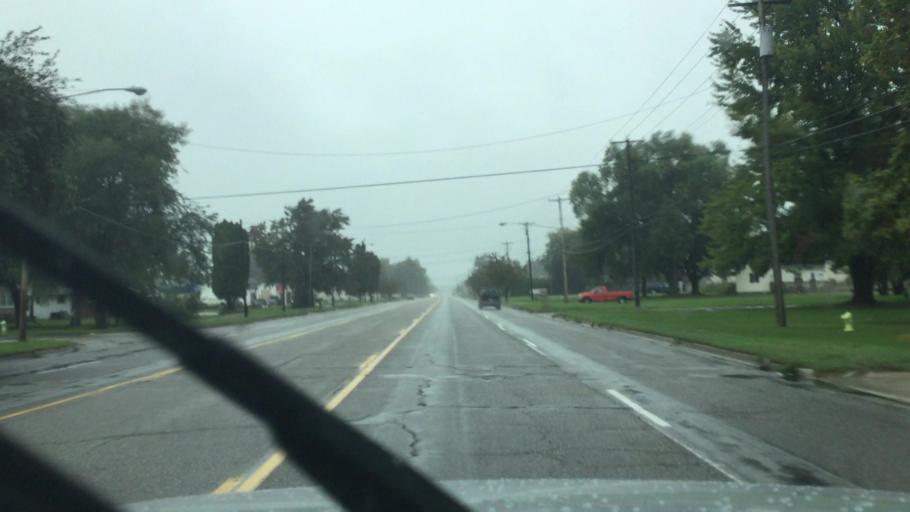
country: US
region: Michigan
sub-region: Saginaw County
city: Bridgeport
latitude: 43.3827
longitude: -83.8991
